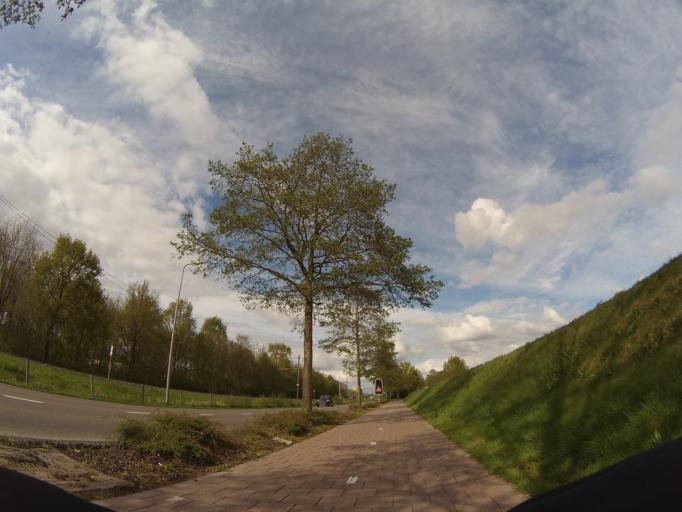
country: NL
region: Drenthe
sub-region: Gemeente Coevorden
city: Coevorden
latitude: 52.6716
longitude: 6.7423
